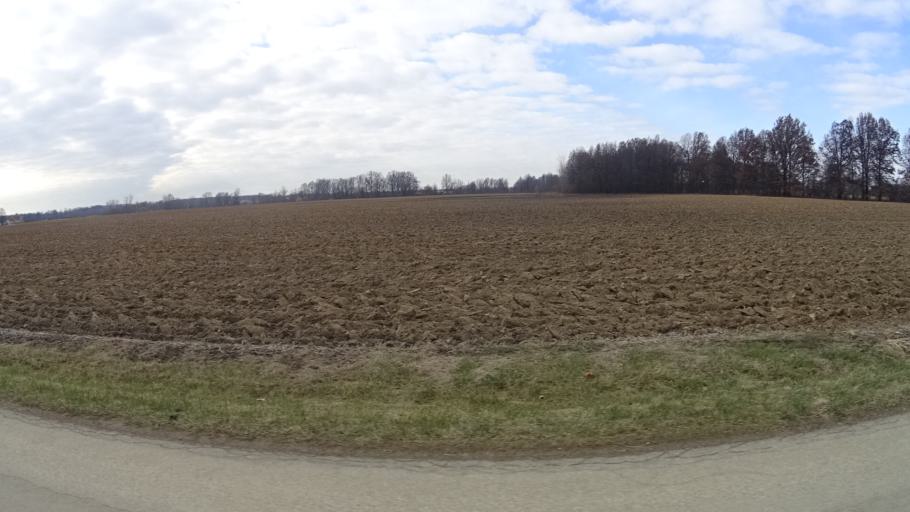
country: US
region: Ohio
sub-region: Lorain County
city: Camden
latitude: 41.2591
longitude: -82.3417
